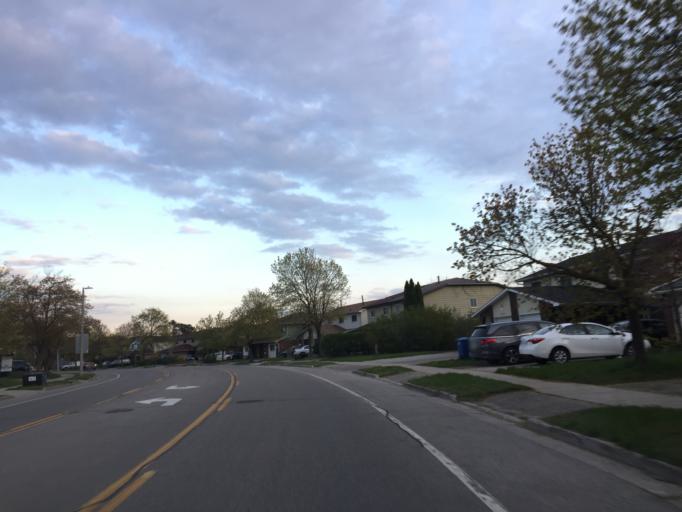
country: CA
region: Ontario
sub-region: Wellington County
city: Guelph
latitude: 43.5135
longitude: -80.2562
